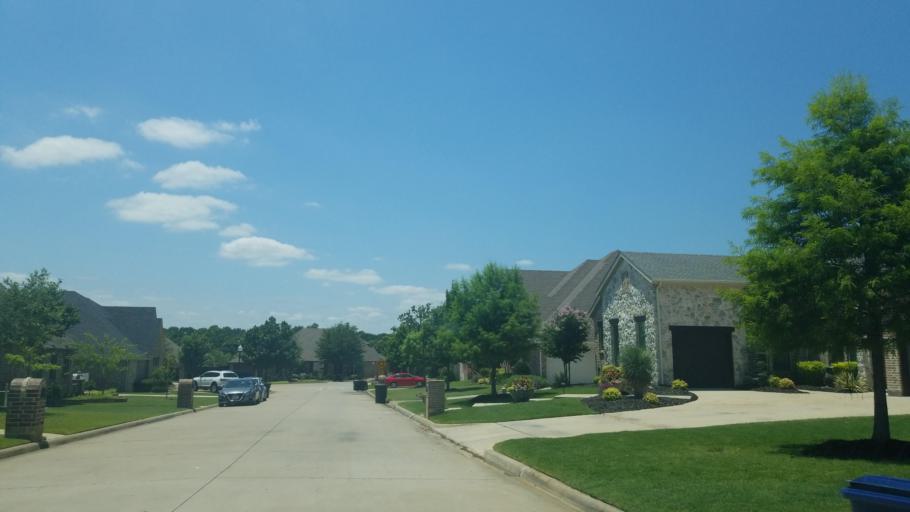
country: US
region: Texas
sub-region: Denton County
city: Copper Canyon
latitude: 33.0812
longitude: -97.0825
